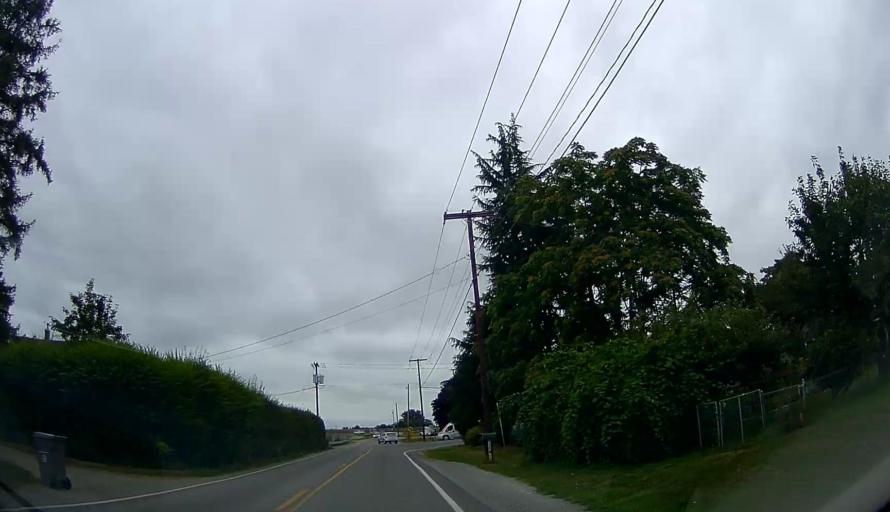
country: US
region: Washington
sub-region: Skagit County
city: Mount Vernon
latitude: 48.4513
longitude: -122.3572
